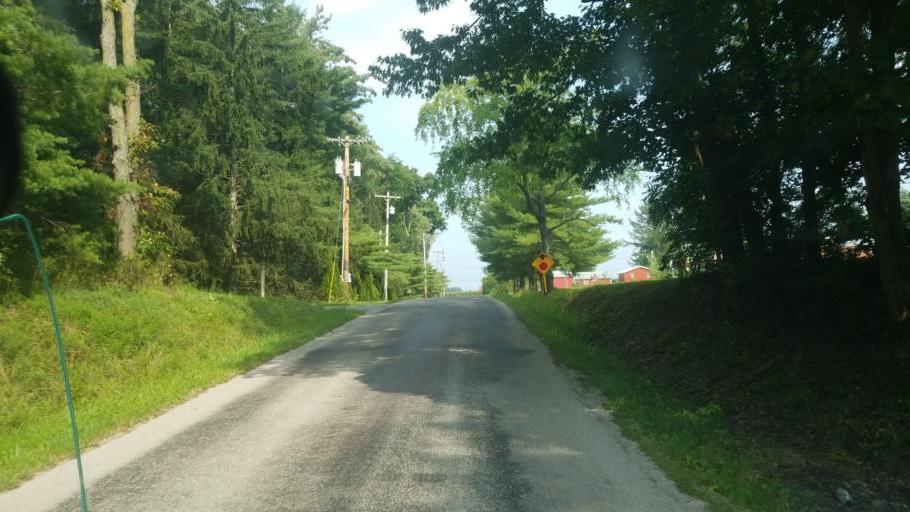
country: US
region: Ohio
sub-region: Lorain County
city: Wellington
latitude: 41.1295
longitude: -82.1252
